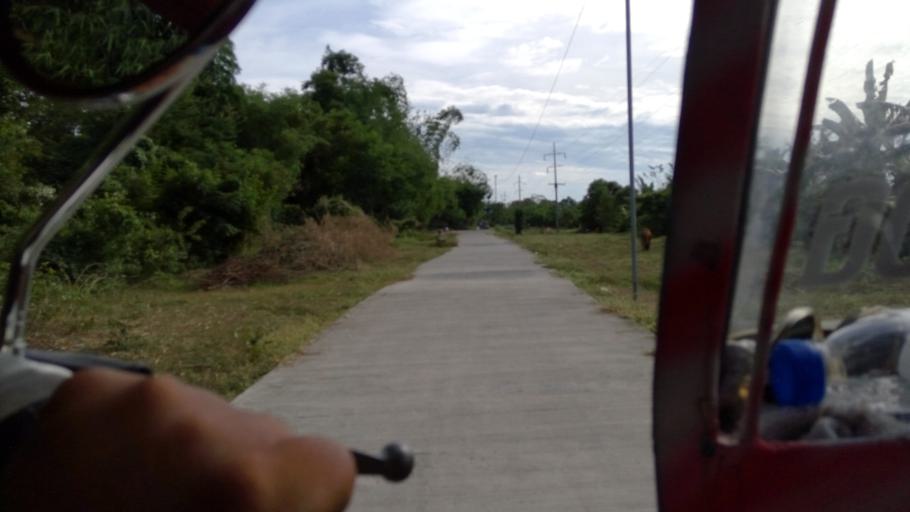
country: PH
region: Ilocos
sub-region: Province of La Union
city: San Eugenio
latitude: 16.3692
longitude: 120.3524
